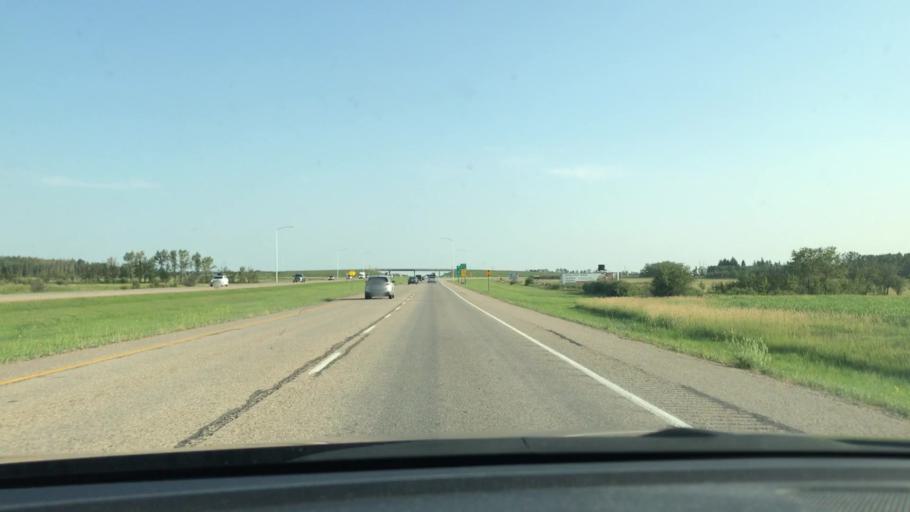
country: CA
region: Alberta
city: Millet
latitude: 53.0979
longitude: -113.5984
